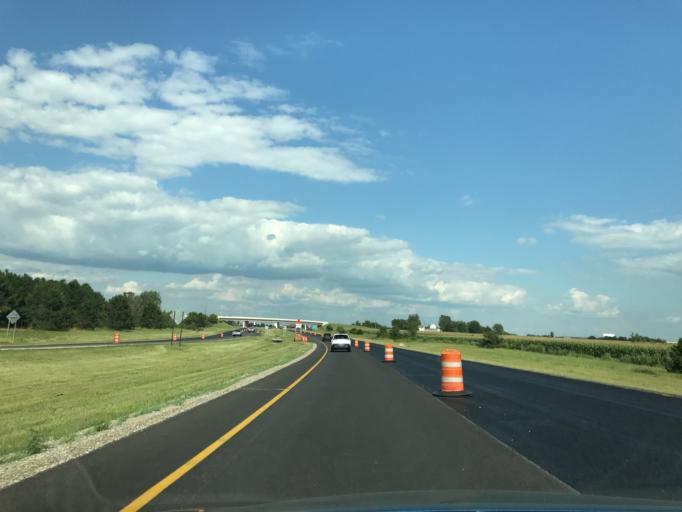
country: US
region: Ohio
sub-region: Allen County
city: Delphos
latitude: 40.8702
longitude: -84.4538
